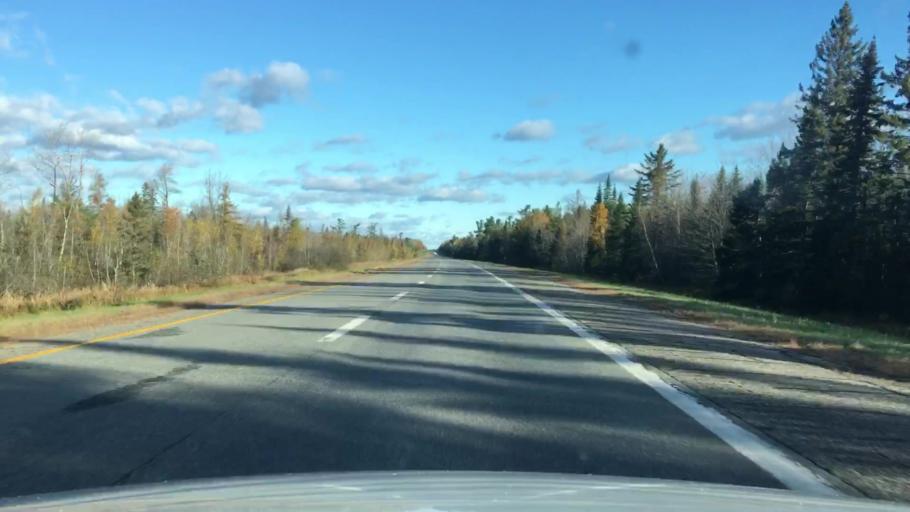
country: US
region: Maine
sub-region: Penobscot County
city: Greenbush
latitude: 45.0551
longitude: -68.6875
